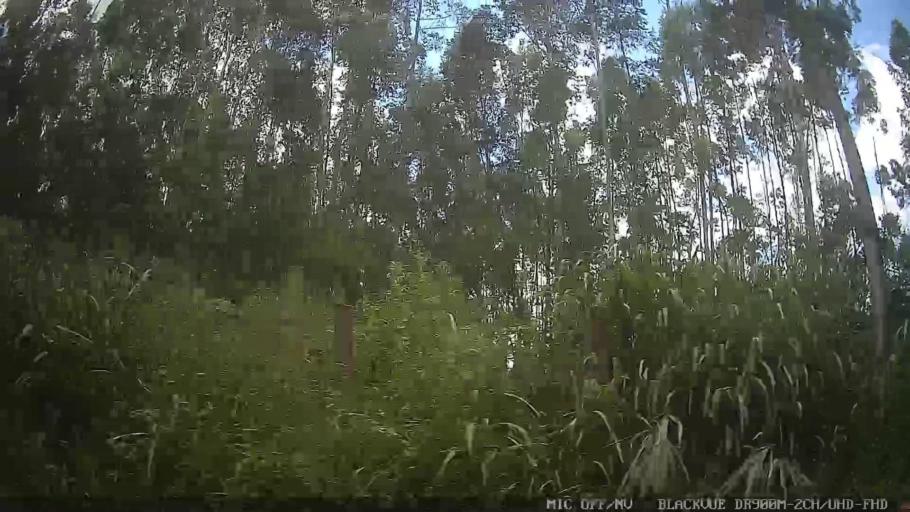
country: BR
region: Sao Paulo
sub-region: Braganca Paulista
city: Braganca Paulista
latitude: -22.9998
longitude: -46.4847
